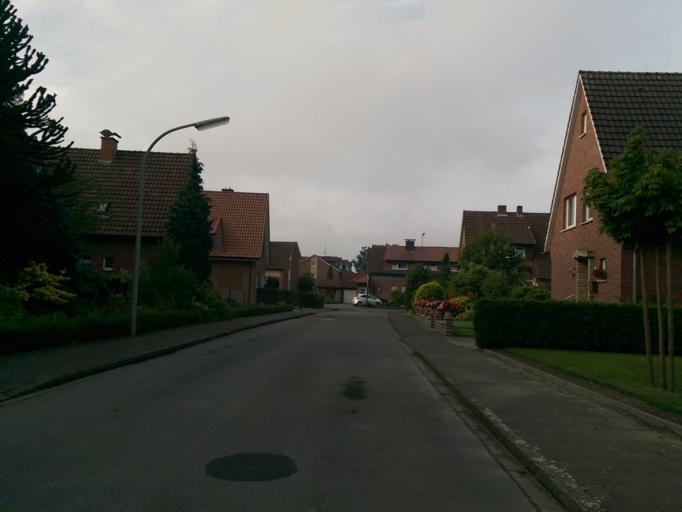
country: DE
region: North Rhine-Westphalia
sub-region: Regierungsbezirk Detmold
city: Harsewinkel
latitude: 51.9502
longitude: 8.2836
